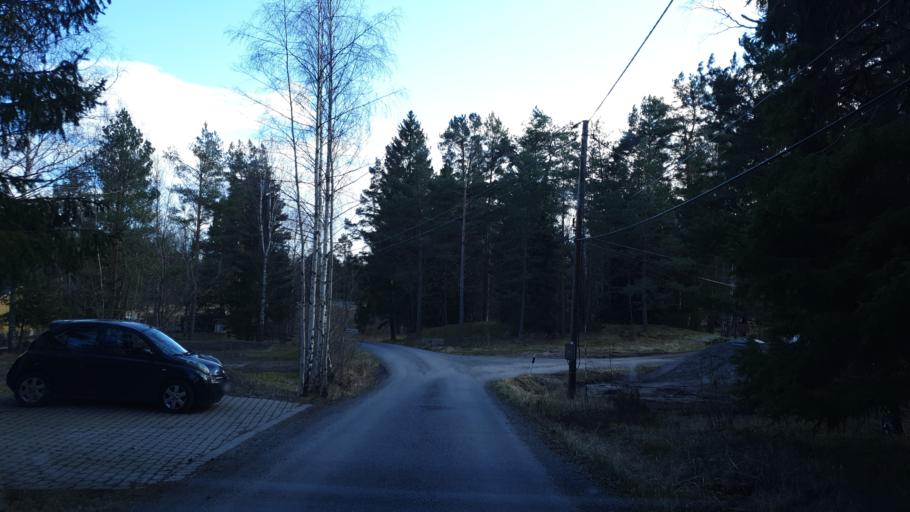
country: SE
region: Stockholm
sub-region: Varmdo Kommun
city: Holo
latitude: 59.2782
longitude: 18.6355
